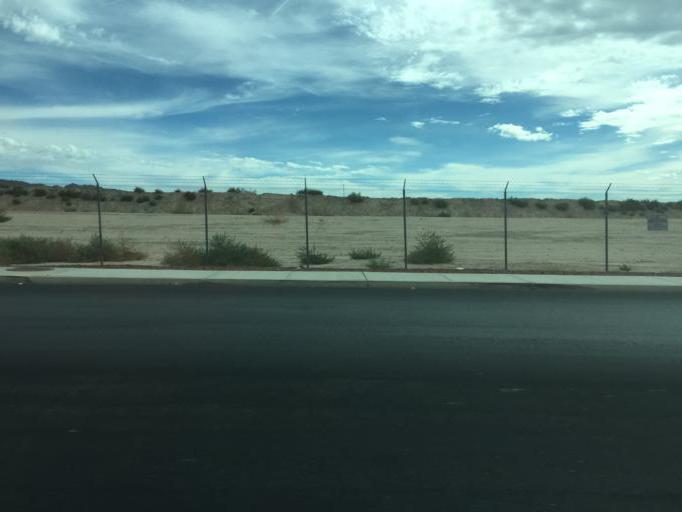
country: US
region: Nevada
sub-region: Clark County
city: Whitney
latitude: 36.1276
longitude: -115.0382
